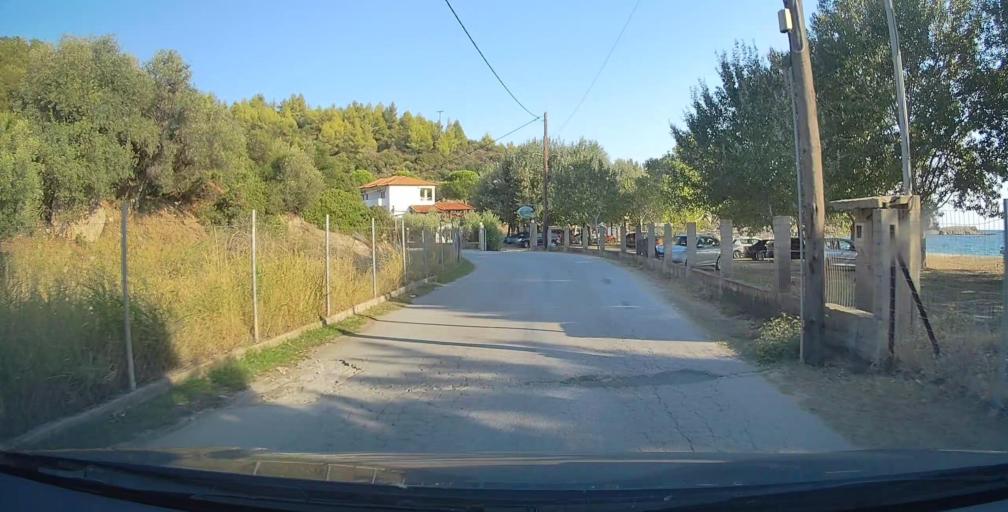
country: GR
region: Central Macedonia
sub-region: Nomos Chalkidikis
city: Sykia
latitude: 39.9951
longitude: 23.8914
